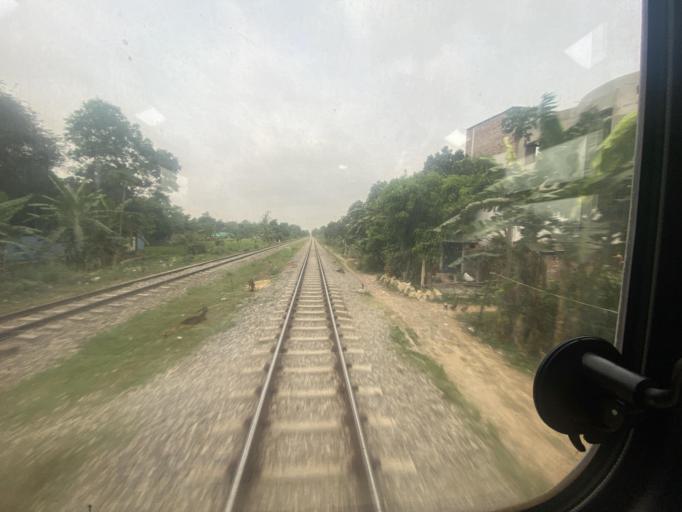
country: BD
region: Dhaka
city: Tungi
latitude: 23.9247
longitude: 90.4469
